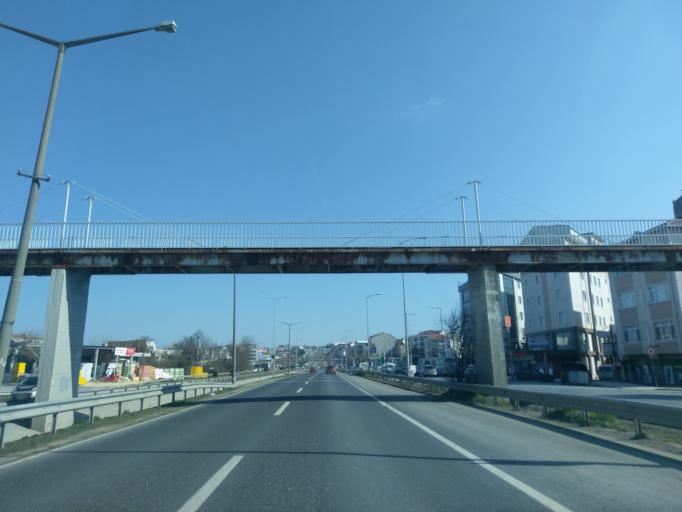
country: TR
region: Istanbul
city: Silivri
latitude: 41.0780
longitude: 28.2433
